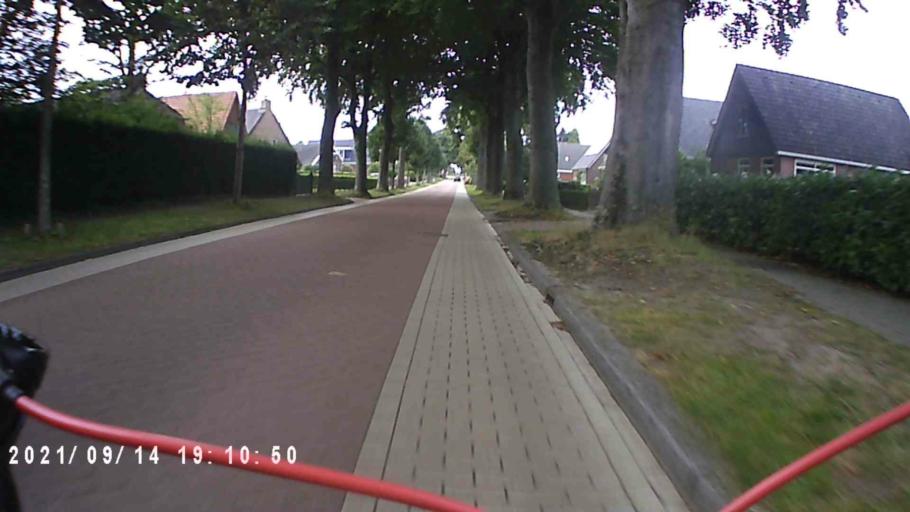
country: NL
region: Drenthe
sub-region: Gemeente Aa en Hunze
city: Anloo
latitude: 53.0606
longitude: 6.7182
